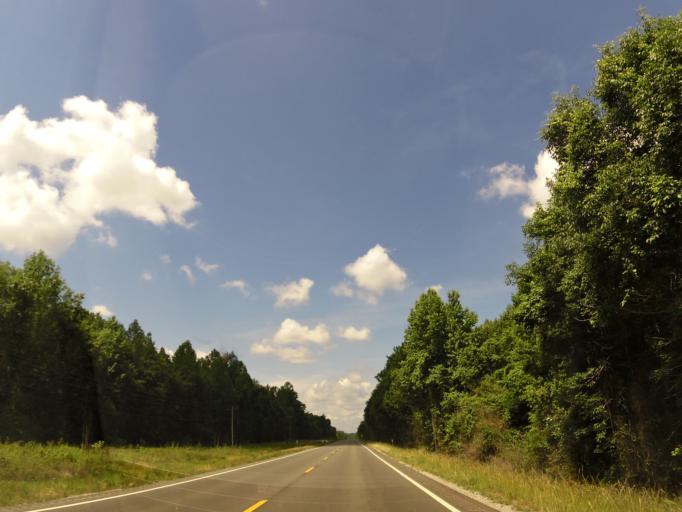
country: US
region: Alabama
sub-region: Marion County
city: Guin
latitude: 33.9466
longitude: -87.9865
